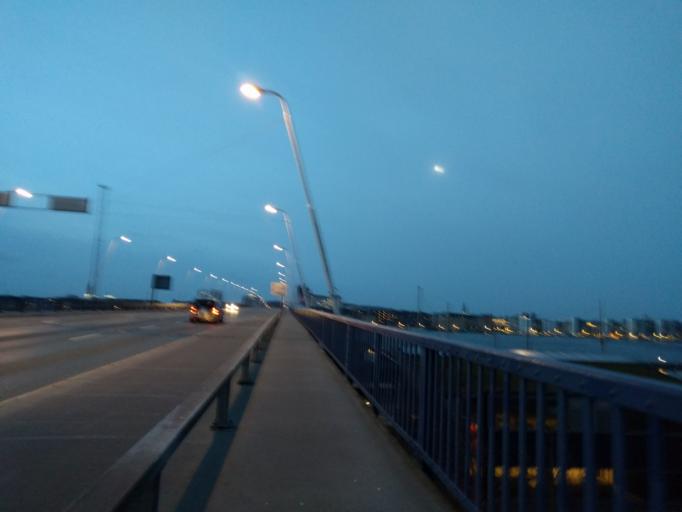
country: DK
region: North Denmark
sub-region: Alborg Kommune
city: Aalborg
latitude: 57.0569
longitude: 9.9220
